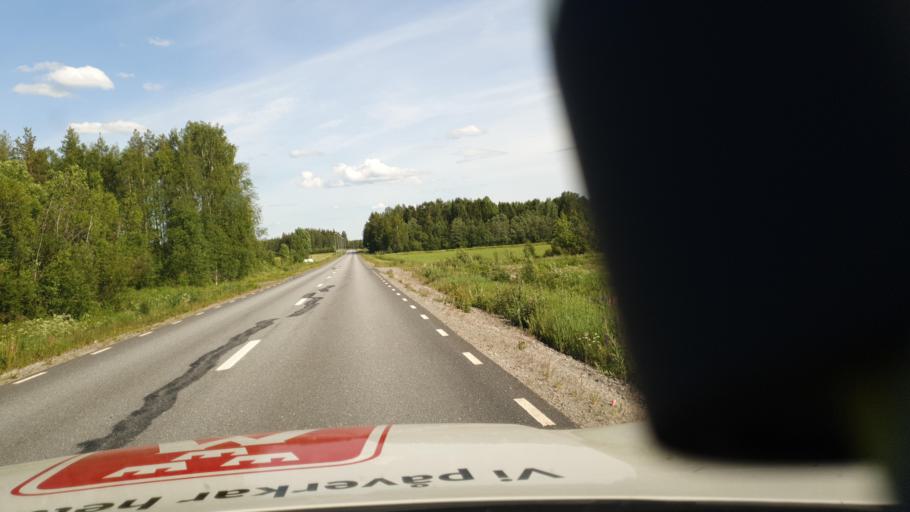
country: SE
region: Vaesterbotten
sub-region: Skelleftea Kommun
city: Forsbacka
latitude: 64.6970
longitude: 20.4806
